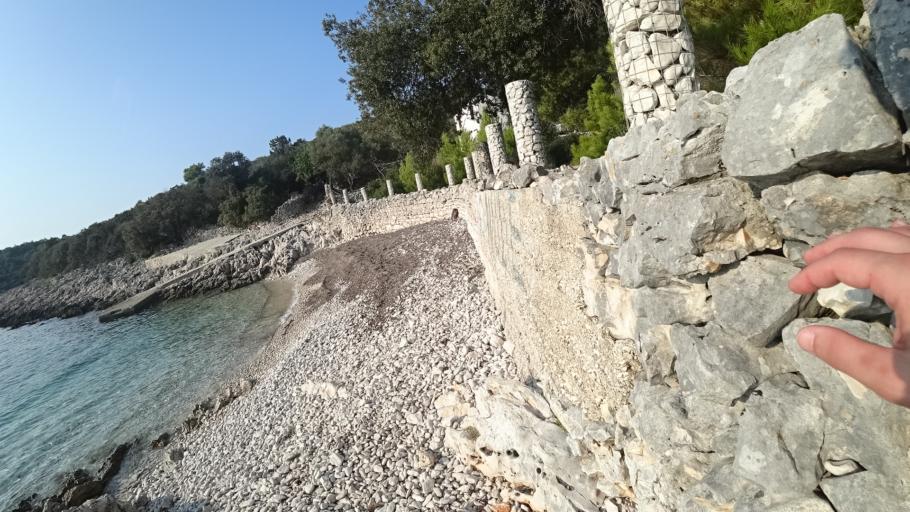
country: HR
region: Primorsko-Goranska
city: Mali Losinj
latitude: 44.5109
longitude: 14.4830
